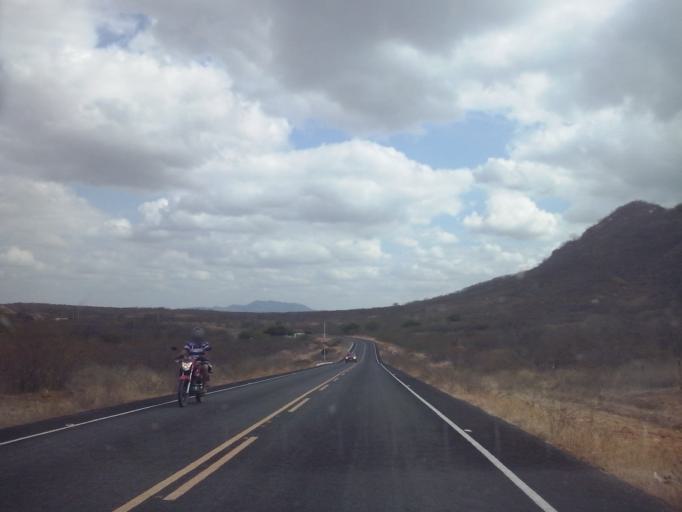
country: BR
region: Paraiba
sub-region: Pombal
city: Pombal
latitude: -6.8799
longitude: -37.5325
